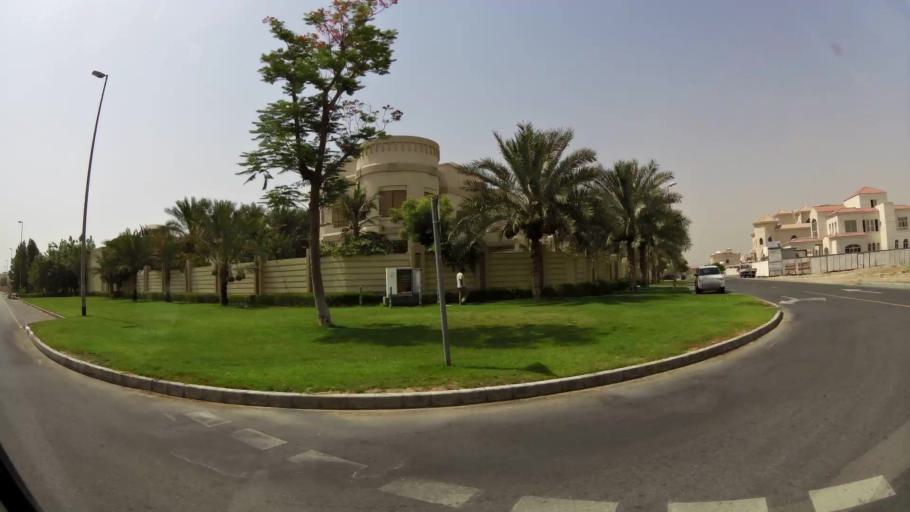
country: AE
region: Ash Shariqah
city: Sharjah
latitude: 25.2551
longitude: 55.4787
